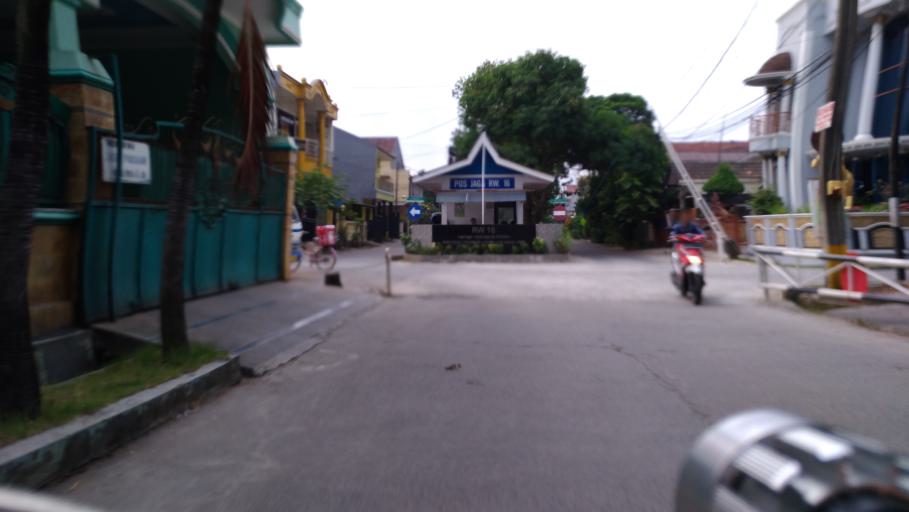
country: ID
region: West Java
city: Depok
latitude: -6.3629
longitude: 106.8648
